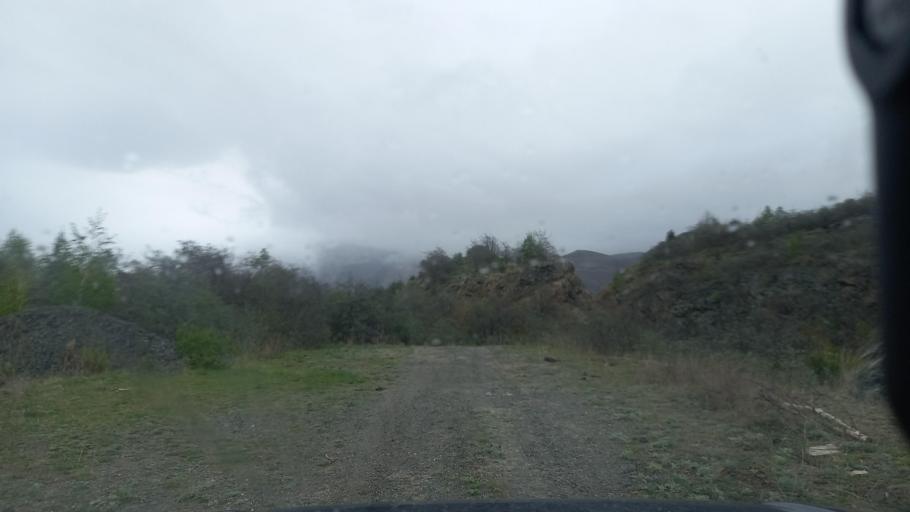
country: RU
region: Kabardino-Balkariya
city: Bylym
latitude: 43.4562
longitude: 43.0039
